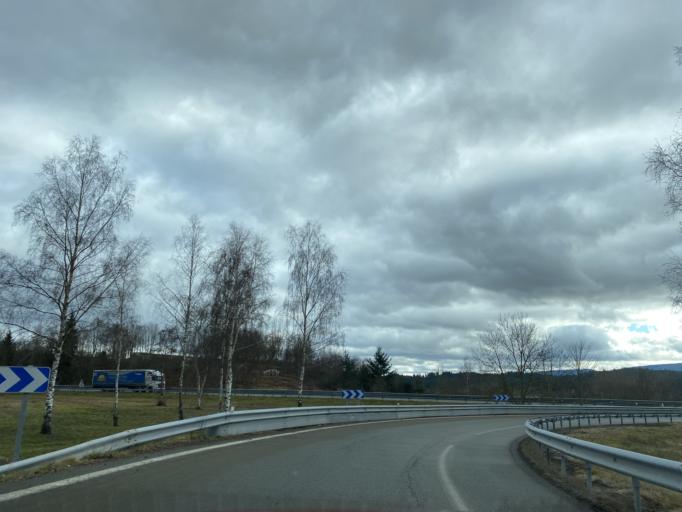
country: FR
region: Rhone-Alpes
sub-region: Departement de la Loire
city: Noiretable
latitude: 45.8545
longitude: 3.7932
